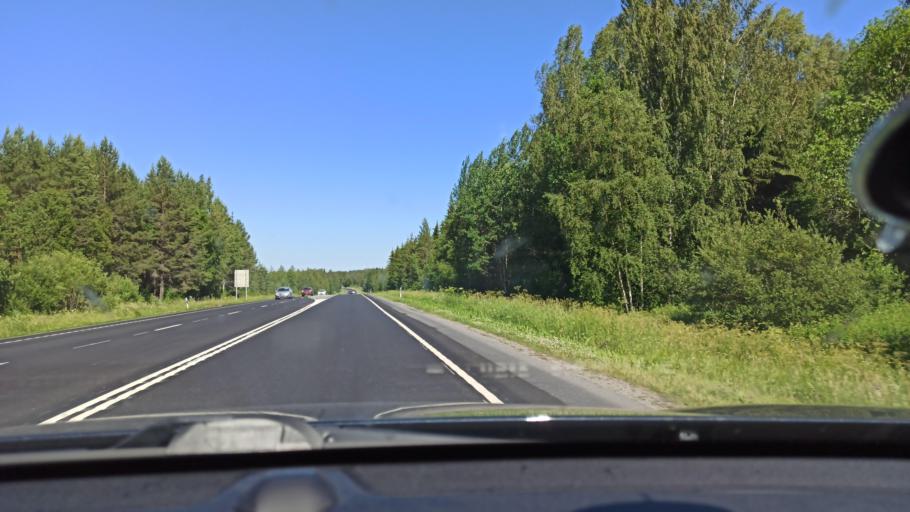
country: FI
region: Ostrobothnia
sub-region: Vaasa
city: Oravais
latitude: 63.2775
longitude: 22.3388
